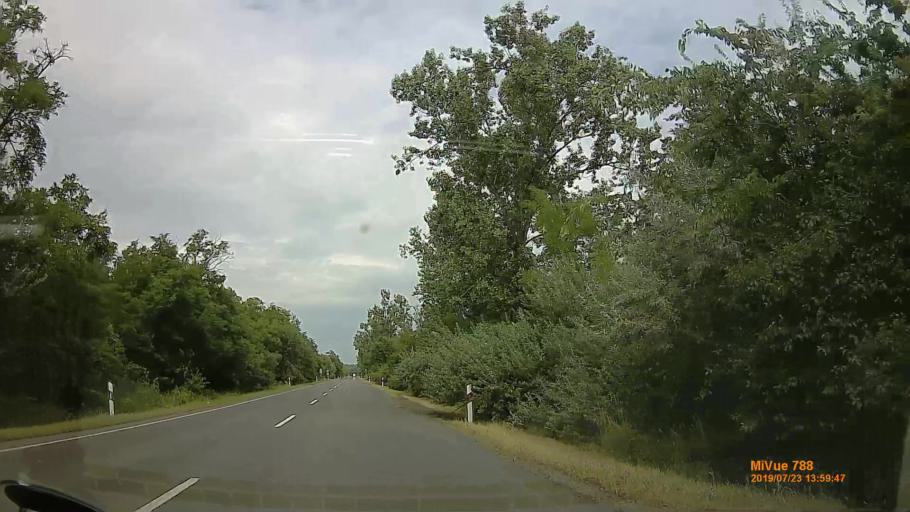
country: HU
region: Szabolcs-Szatmar-Bereg
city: Tiszavasvari
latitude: 47.9299
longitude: 21.2981
